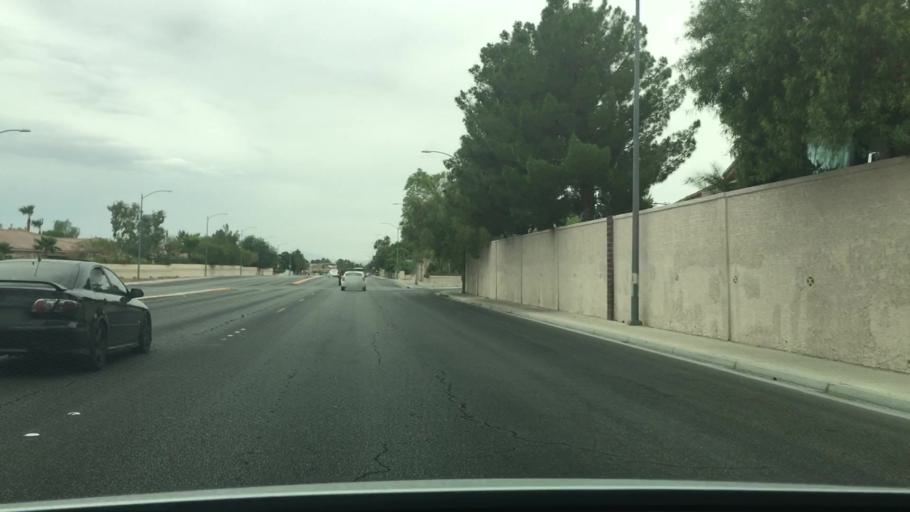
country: US
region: Nevada
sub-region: Clark County
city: Spring Valley
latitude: 36.1481
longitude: -115.2614
